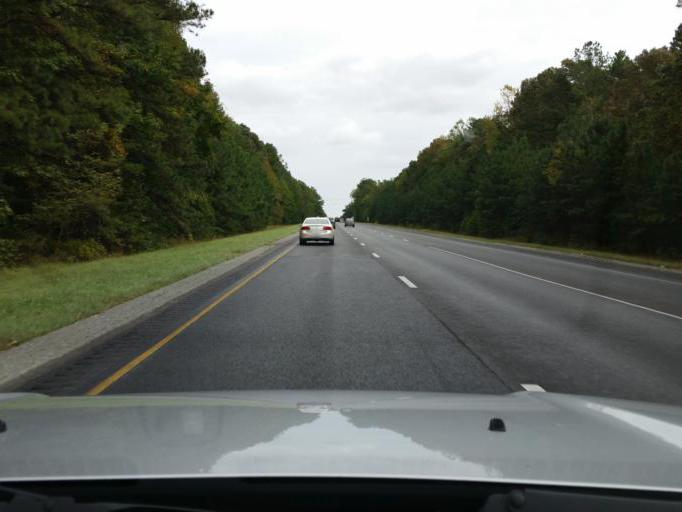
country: US
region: Virginia
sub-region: New Kent County
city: New Kent
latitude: 37.4946
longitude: -77.0193
